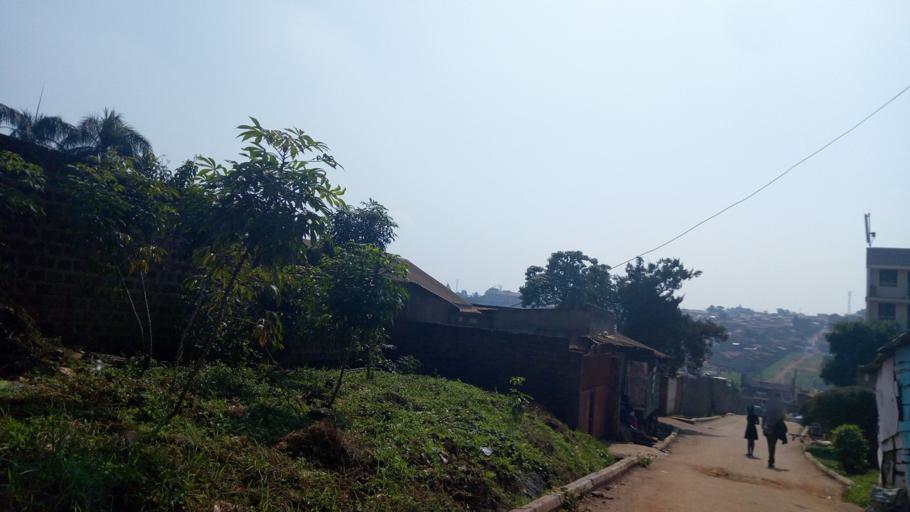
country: UG
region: Central Region
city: Kampala Central Division
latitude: 0.3402
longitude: 32.5697
